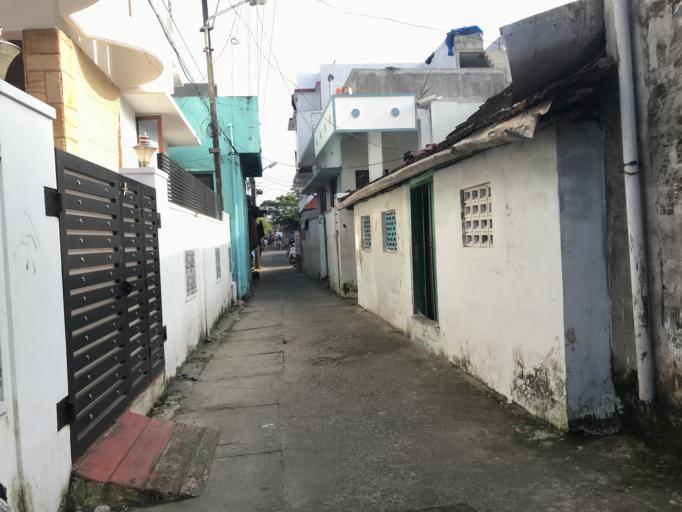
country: IN
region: Kerala
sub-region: Ernakulam
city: Cochin
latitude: 9.9675
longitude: 76.2486
